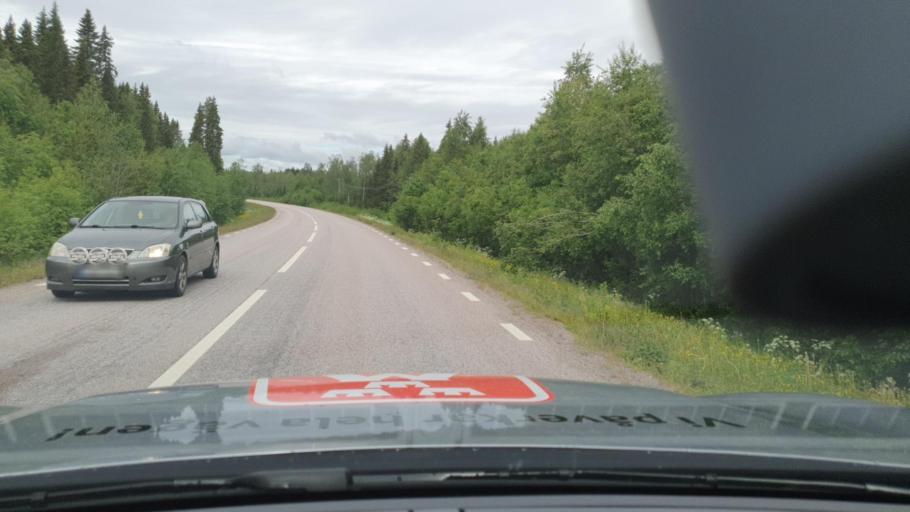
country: SE
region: Norrbotten
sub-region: Lulea Kommun
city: Ranea
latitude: 65.8707
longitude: 22.2993
